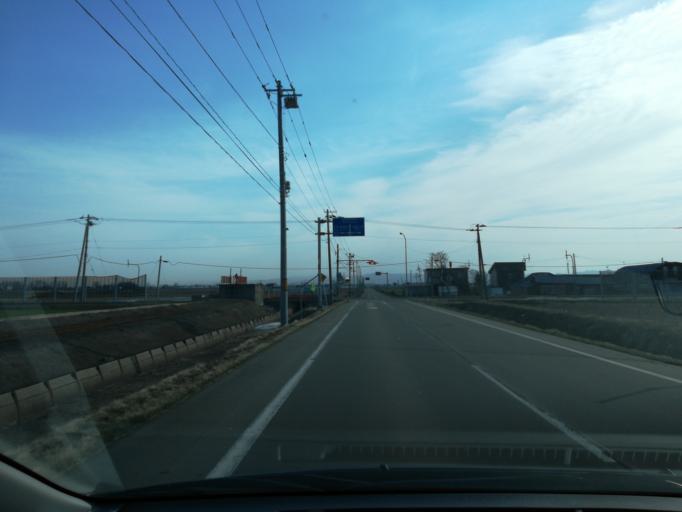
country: JP
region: Hokkaido
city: Iwamizawa
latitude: 43.1858
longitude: 141.6984
